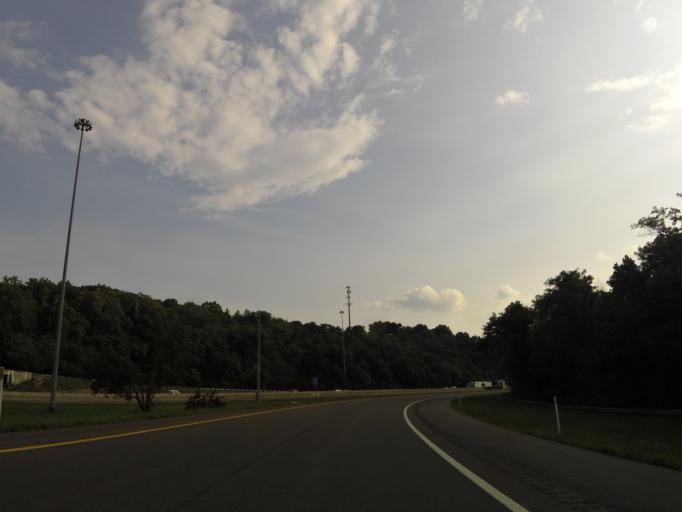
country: US
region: Tennessee
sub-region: Knox County
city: Knoxville
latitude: 36.0136
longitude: -83.8618
